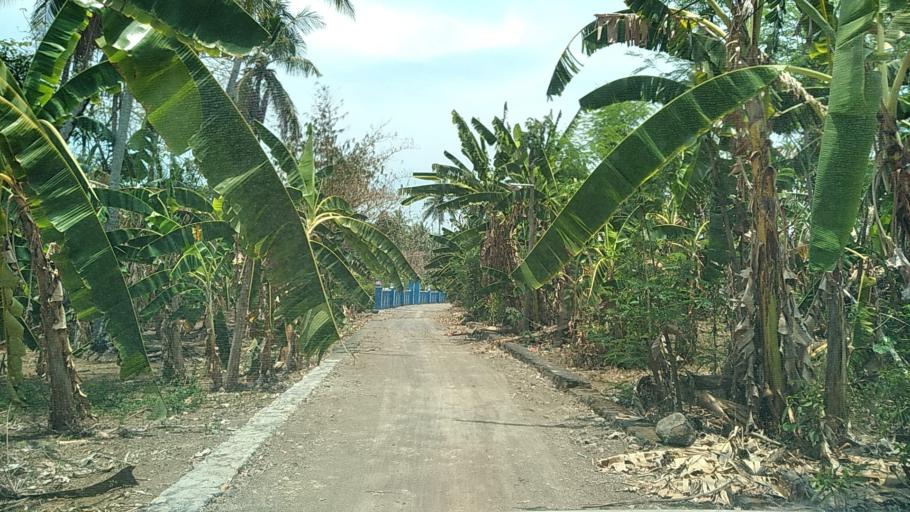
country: ID
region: Central Java
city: Mranggen
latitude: -6.9889
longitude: 110.4941
